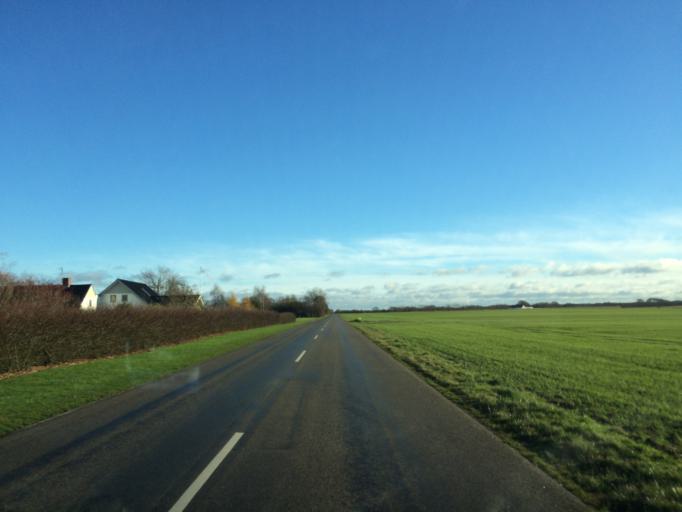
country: DK
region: Central Jutland
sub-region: Herning Kommune
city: Kibaek
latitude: 56.0645
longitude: 8.7592
